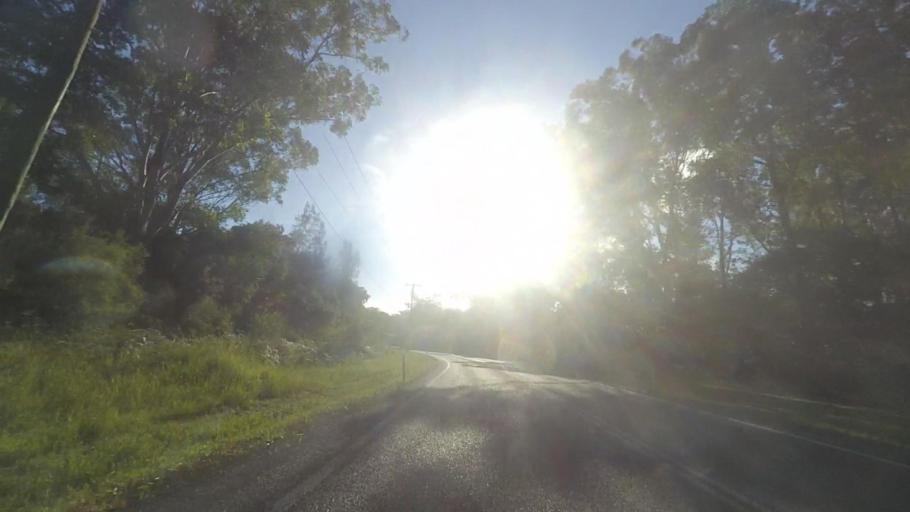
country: AU
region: New South Wales
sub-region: Great Lakes
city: Nabiac
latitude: -32.0894
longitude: 152.4631
